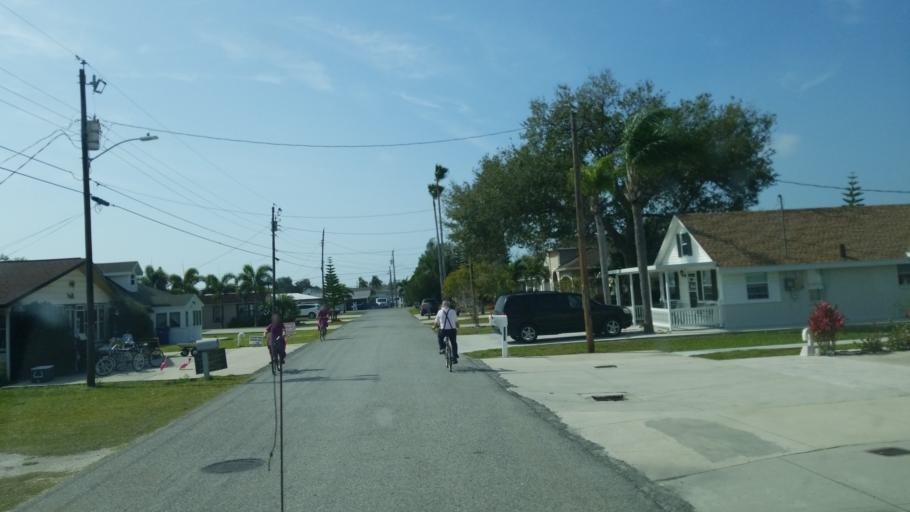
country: US
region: Florida
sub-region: Sarasota County
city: Southgate
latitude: 27.3212
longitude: -82.5004
